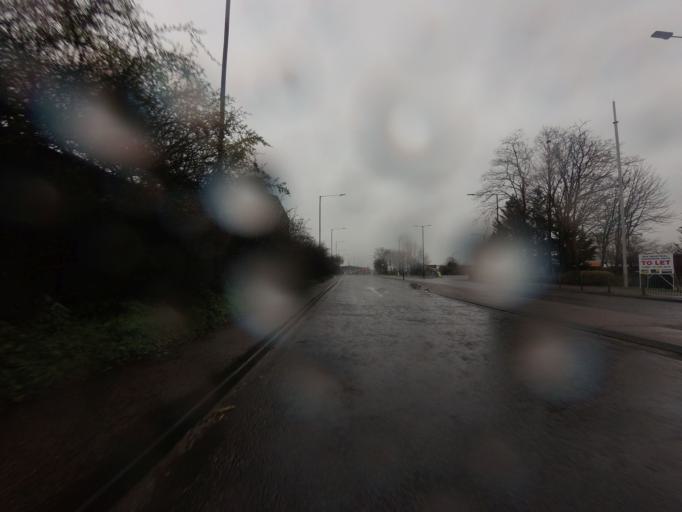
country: GB
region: England
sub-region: Hertfordshire
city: Waltham Cross
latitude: 51.6597
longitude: -0.0297
